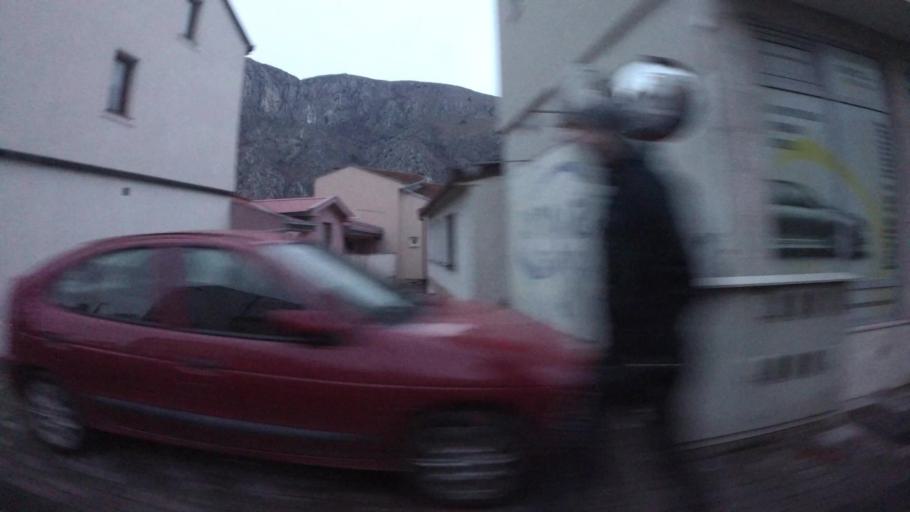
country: BA
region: Federation of Bosnia and Herzegovina
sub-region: Hercegovacko-Bosanski Kanton
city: Mostar
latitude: 43.3322
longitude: 17.8182
